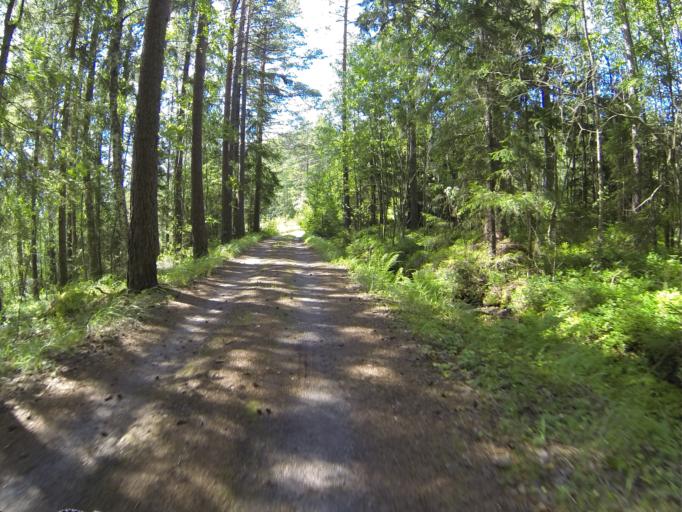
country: FI
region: Varsinais-Suomi
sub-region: Salo
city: Pernioe
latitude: 60.2818
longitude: 23.0470
